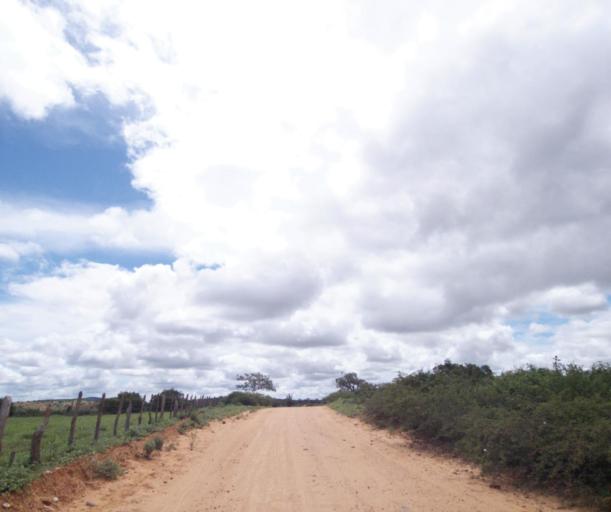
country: BR
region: Bahia
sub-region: Tanhacu
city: Tanhacu
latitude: -14.1552
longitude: -41.1949
